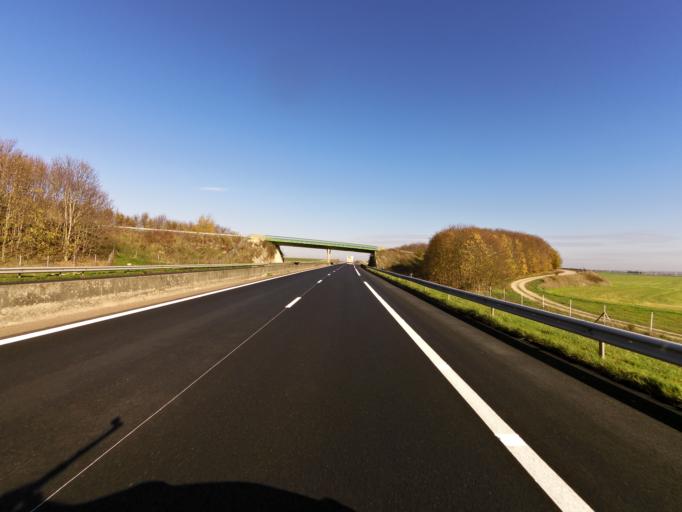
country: FR
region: Champagne-Ardenne
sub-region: Departement de la Marne
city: Fagnieres
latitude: 48.9364
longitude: 4.2859
